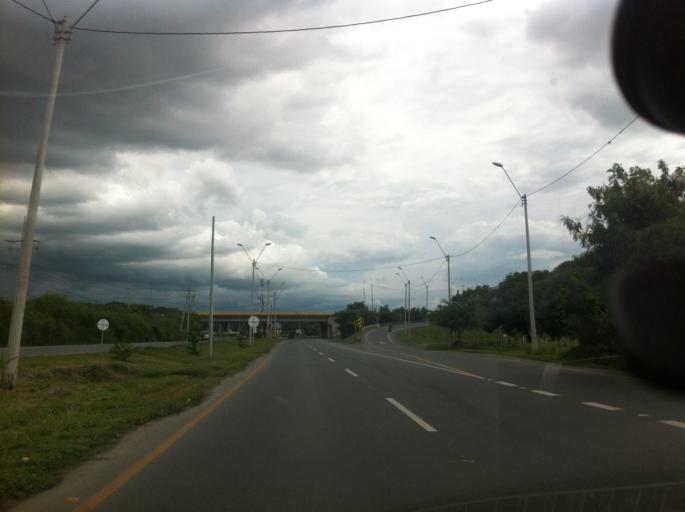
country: CO
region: Valle del Cauca
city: El Cerrito
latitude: 3.7031
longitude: -76.3193
